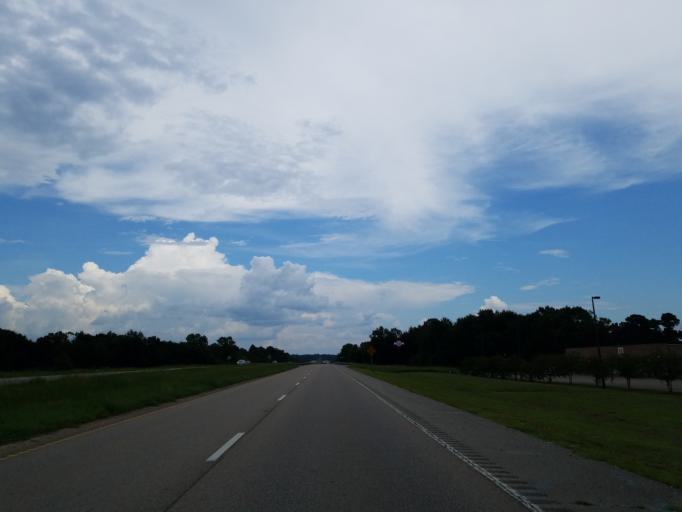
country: US
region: Mississippi
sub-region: Forrest County
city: Glendale
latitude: 31.3596
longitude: -89.2869
